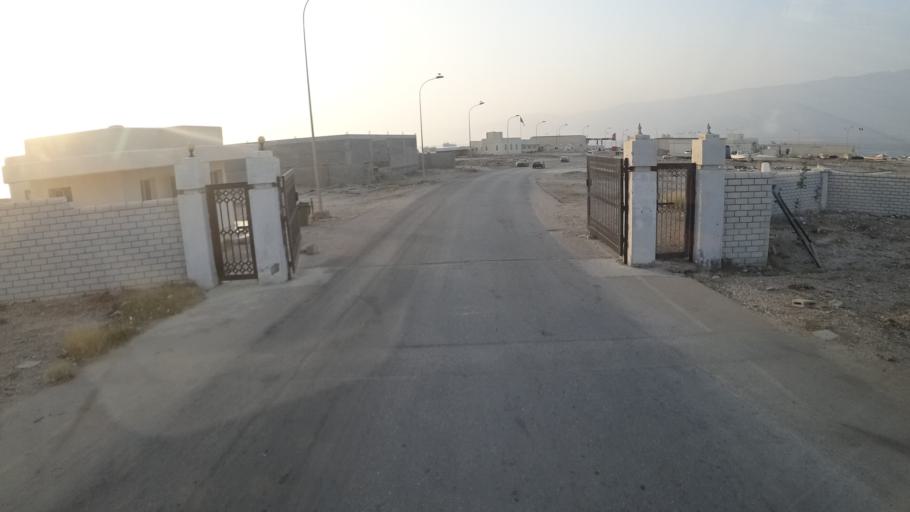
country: OM
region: Zufar
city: Salalah
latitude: 16.9836
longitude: 54.6883
